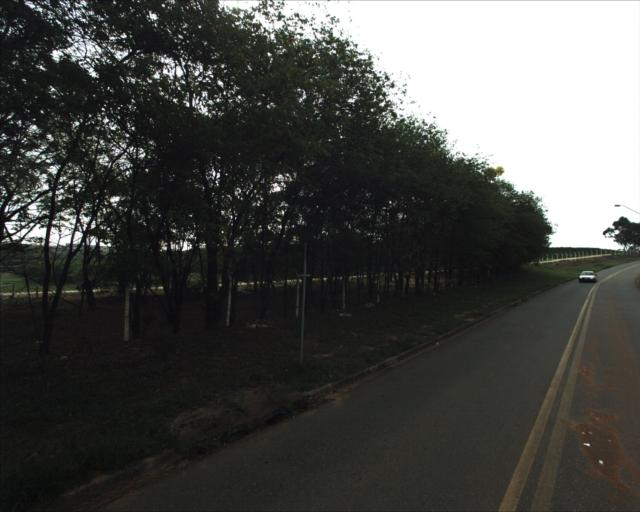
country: BR
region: Sao Paulo
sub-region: Sorocaba
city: Sorocaba
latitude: -23.4604
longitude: -47.4434
